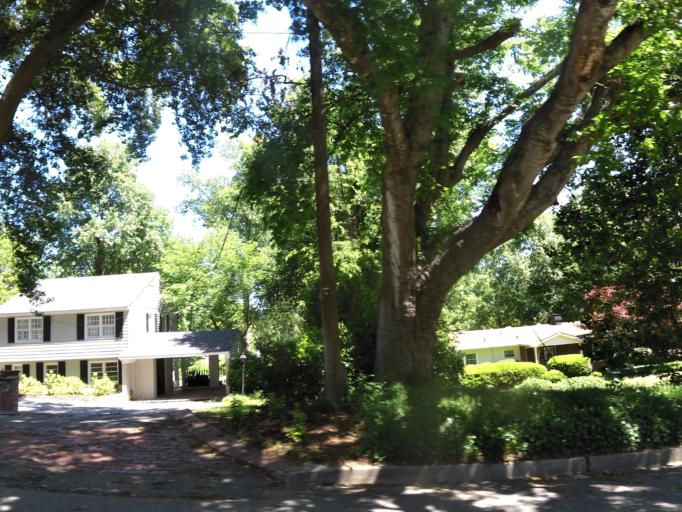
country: US
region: Georgia
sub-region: Columbia County
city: Martinez
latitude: 33.4810
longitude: -82.0346
